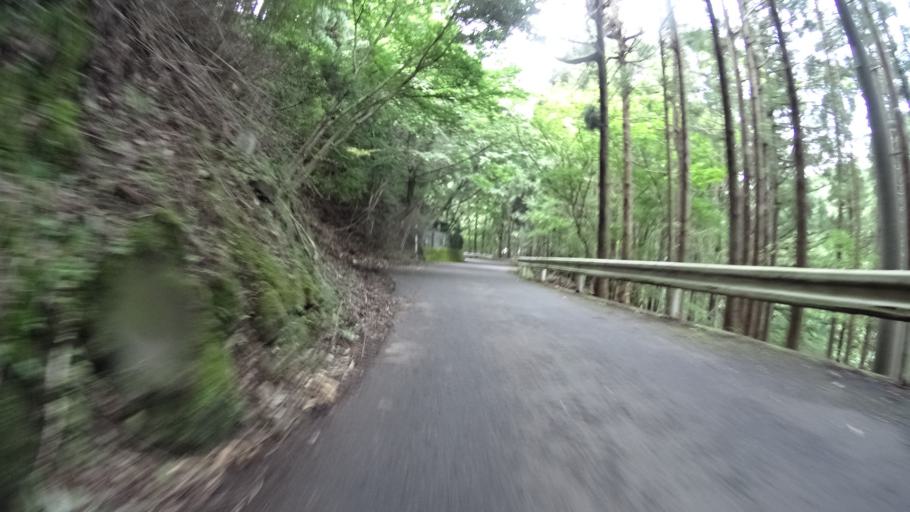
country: JP
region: Kanagawa
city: Hadano
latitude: 35.4964
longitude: 139.2218
